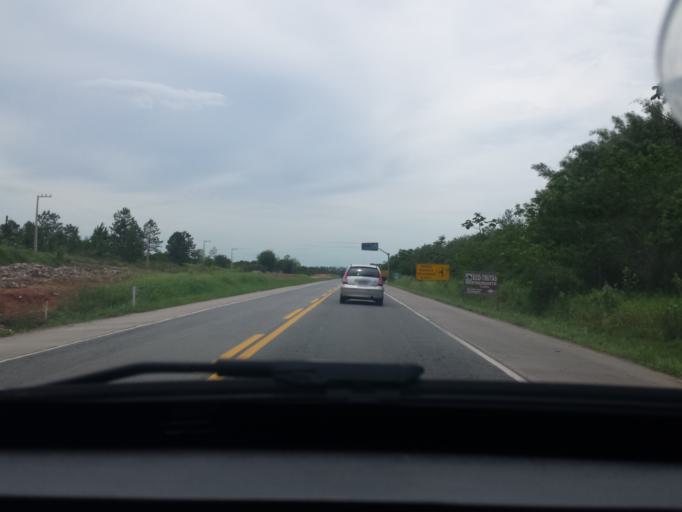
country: BR
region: Santa Catarina
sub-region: Gaspar
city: Gaspar
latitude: -26.8808
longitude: -48.8451
